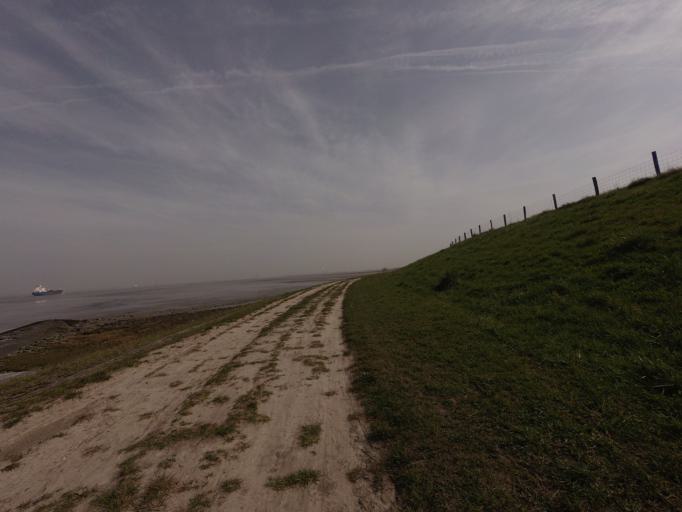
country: NL
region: Zeeland
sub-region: Gemeente Hulst
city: Hulst
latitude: 51.3638
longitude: 4.0858
